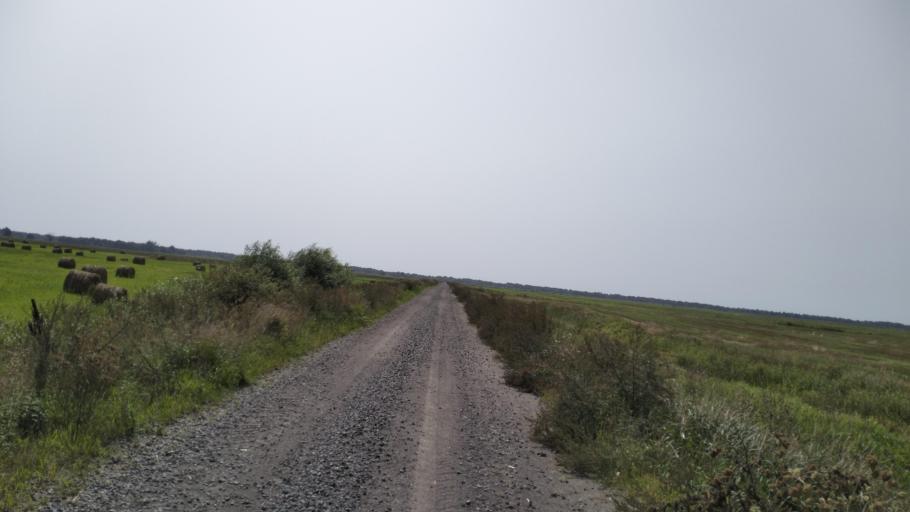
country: BY
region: Brest
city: Davyd-Haradok
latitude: 51.9895
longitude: 27.1758
